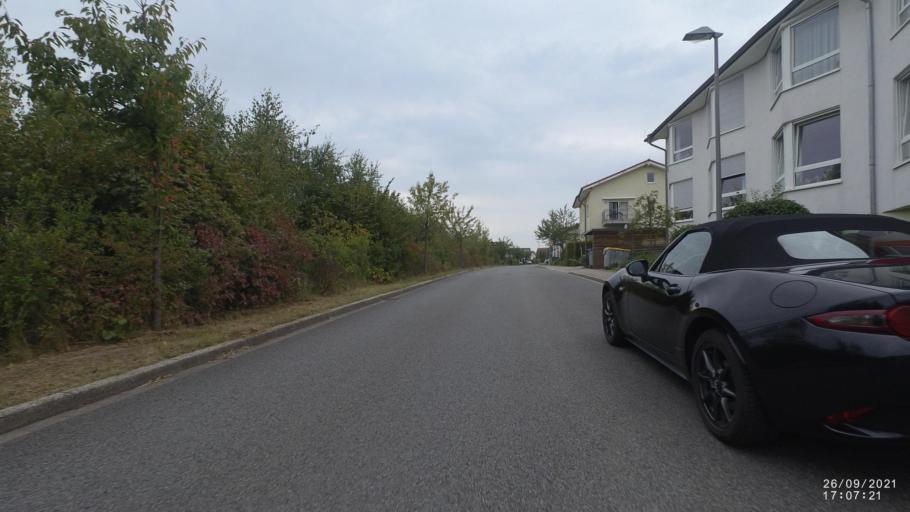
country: DE
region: North Rhine-Westphalia
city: Iserlohn
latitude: 51.4211
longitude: 7.7152
